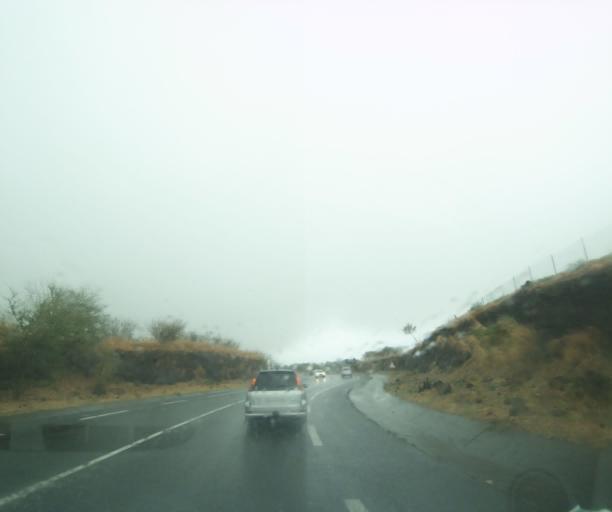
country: RE
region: Reunion
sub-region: Reunion
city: Saint-Paul
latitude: -21.0423
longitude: 55.2484
